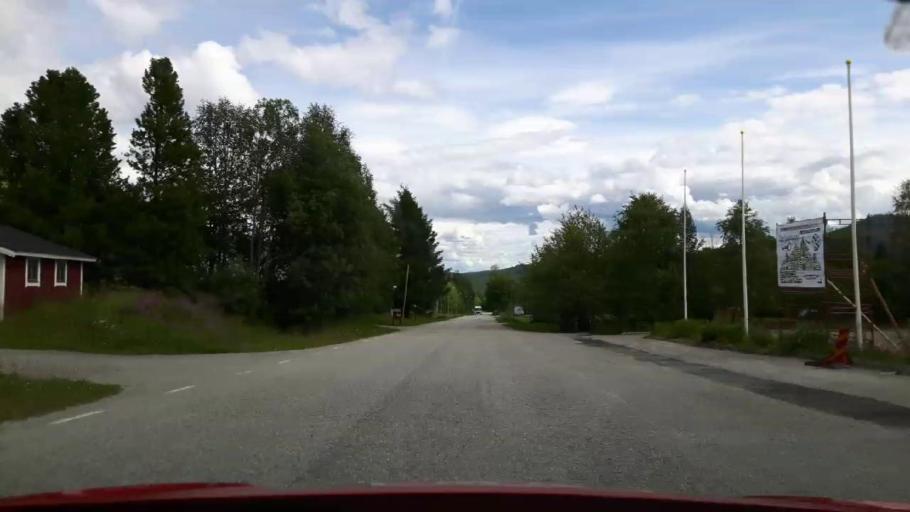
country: NO
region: Hedmark
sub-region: Engerdal
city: Engerdal
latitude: 62.4414
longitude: 12.6853
